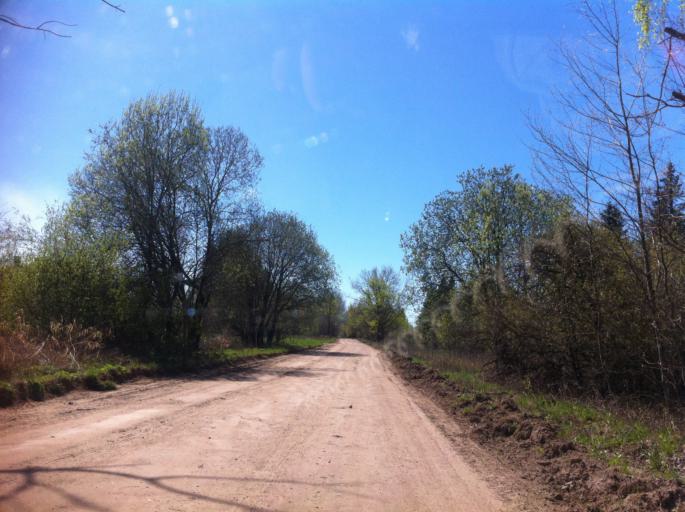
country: RU
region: Pskov
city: Izborsk
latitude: 57.7855
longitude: 27.9626
